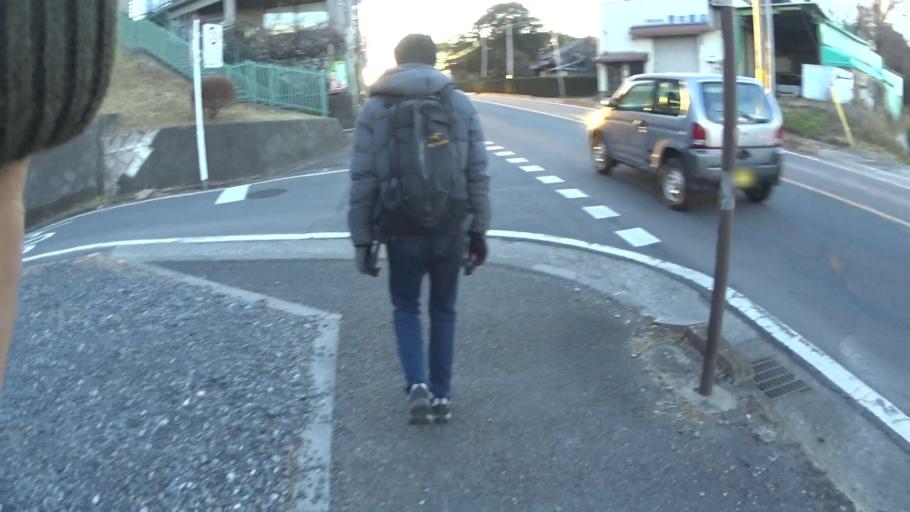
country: JP
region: Saitama
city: Koshigaya
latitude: 35.8839
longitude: 139.7360
